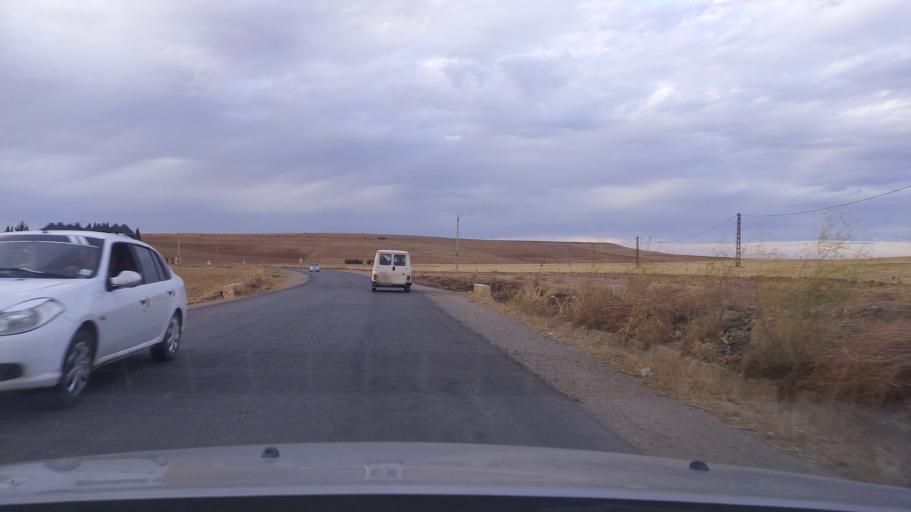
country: DZ
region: Tiaret
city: Frenda
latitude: 35.0241
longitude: 1.0990
